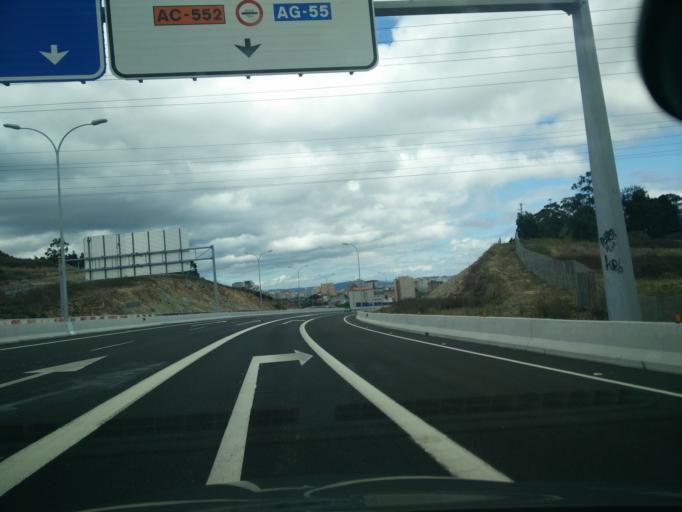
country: ES
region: Galicia
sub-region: Provincia da Coruna
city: A Coruna
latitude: 43.3416
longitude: -8.4219
